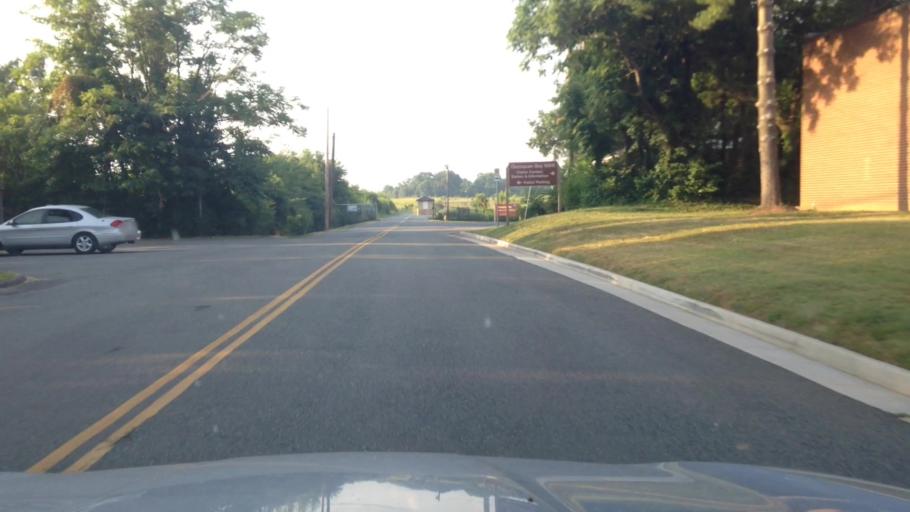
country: US
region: Virginia
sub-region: Prince William County
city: Woodbridge
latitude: 38.6499
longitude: -77.2442
